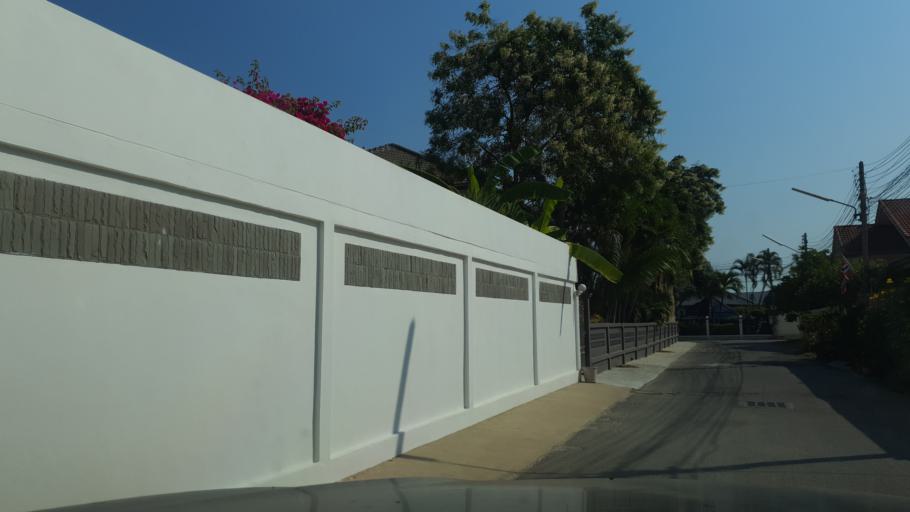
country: TH
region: Prachuap Khiri Khan
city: Hua Hin
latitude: 12.5512
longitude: 99.9544
